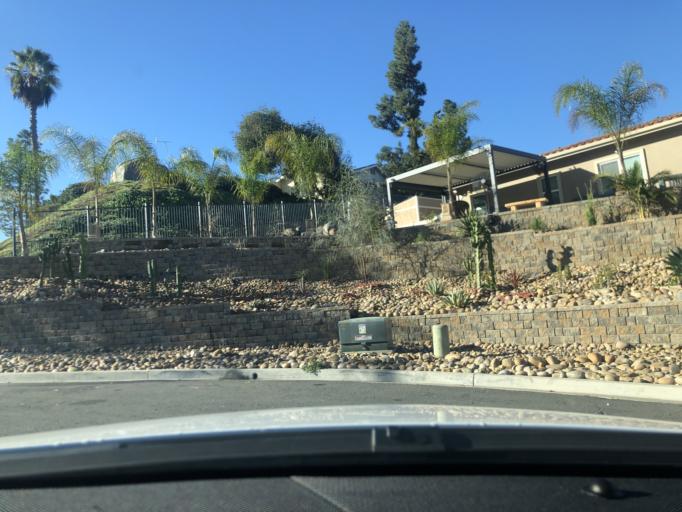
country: US
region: California
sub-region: San Diego County
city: Casa de Oro-Mount Helix
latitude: 32.7692
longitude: -116.9589
